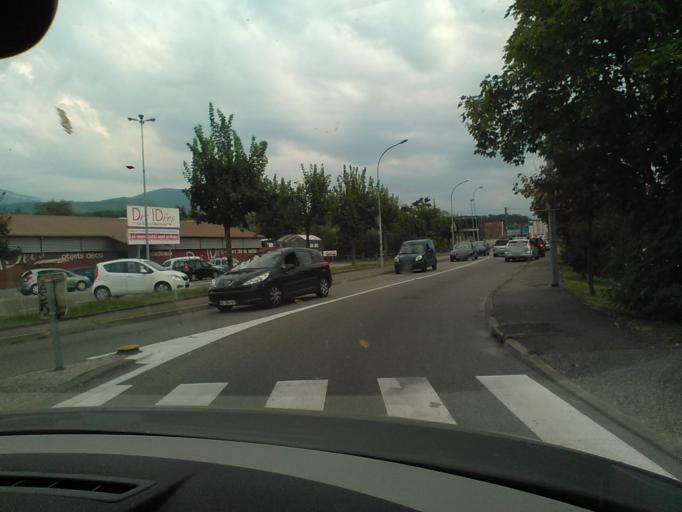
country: FR
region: Rhone-Alpes
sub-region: Departement de la Savoie
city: Saint-Alban-Leysse
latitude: 45.5715
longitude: 5.9481
